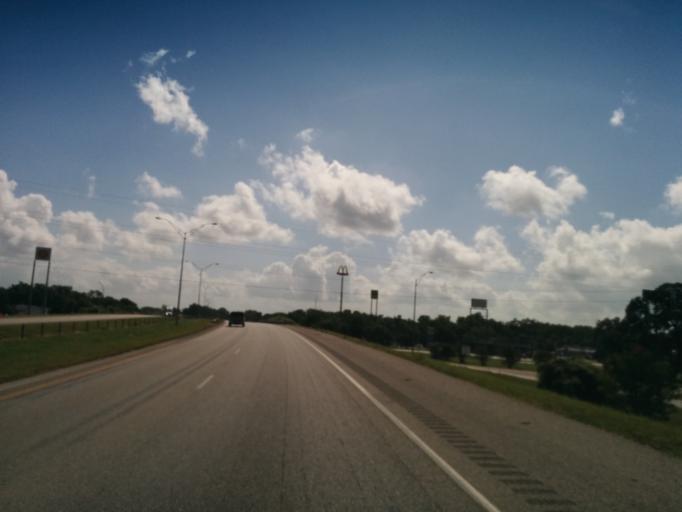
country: US
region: Texas
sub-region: Colorado County
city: Columbus
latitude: 29.6919
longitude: -96.5417
